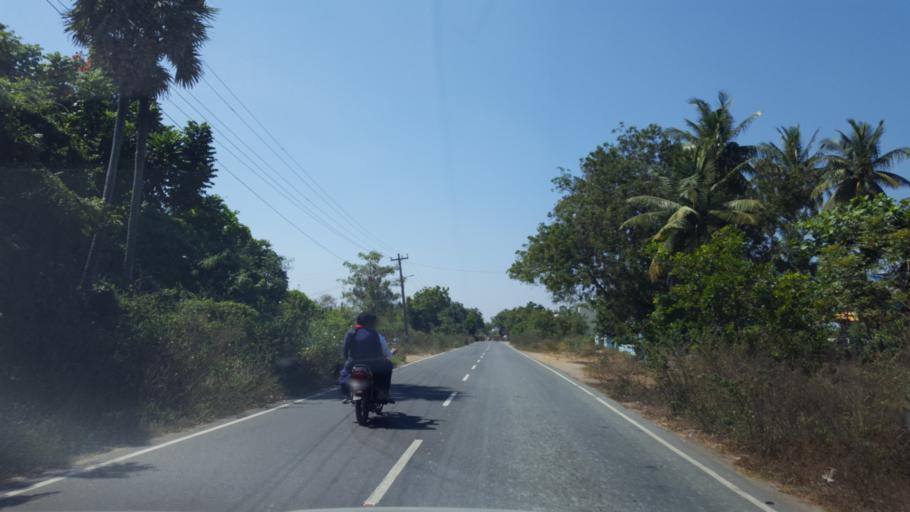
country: IN
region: Tamil Nadu
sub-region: Kancheepuram
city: Wallajahbad
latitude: 12.7664
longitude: 79.9051
